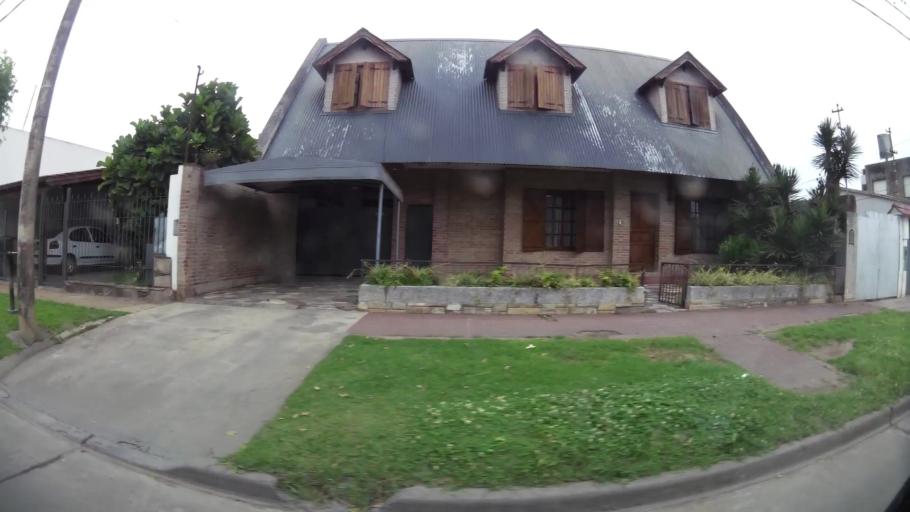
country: AR
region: Buenos Aires
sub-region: Partido de Zarate
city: Zarate
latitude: -34.0975
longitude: -59.0347
